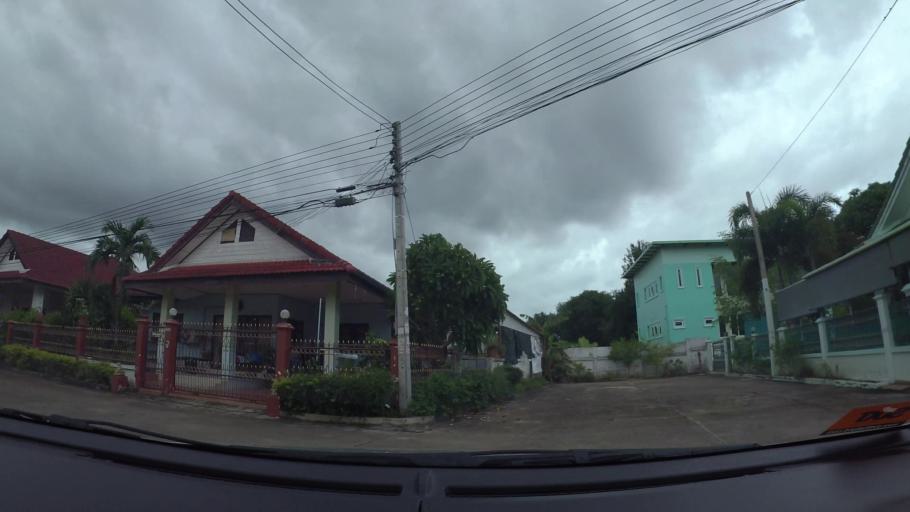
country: TH
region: Chon Buri
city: Sattahip
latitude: 12.7281
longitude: 100.8979
